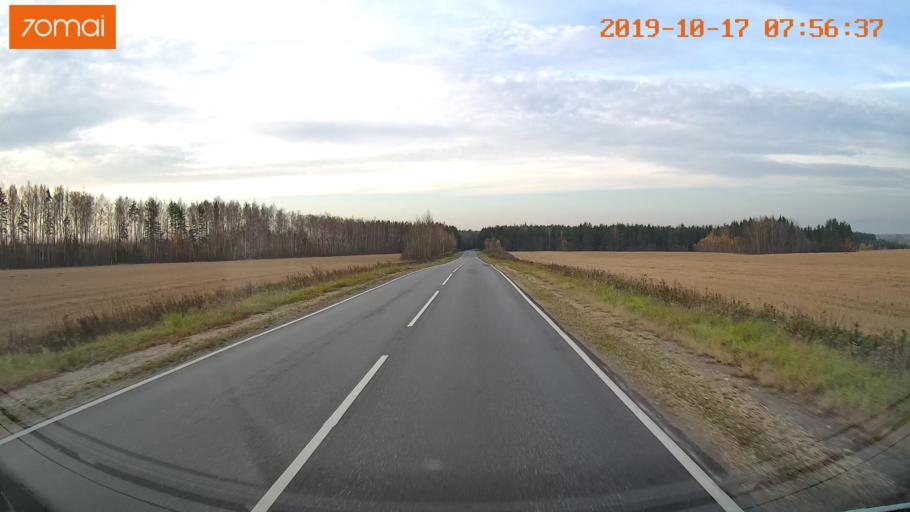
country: RU
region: Vladimir
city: Bavleny
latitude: 56.4208
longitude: 39.5882
